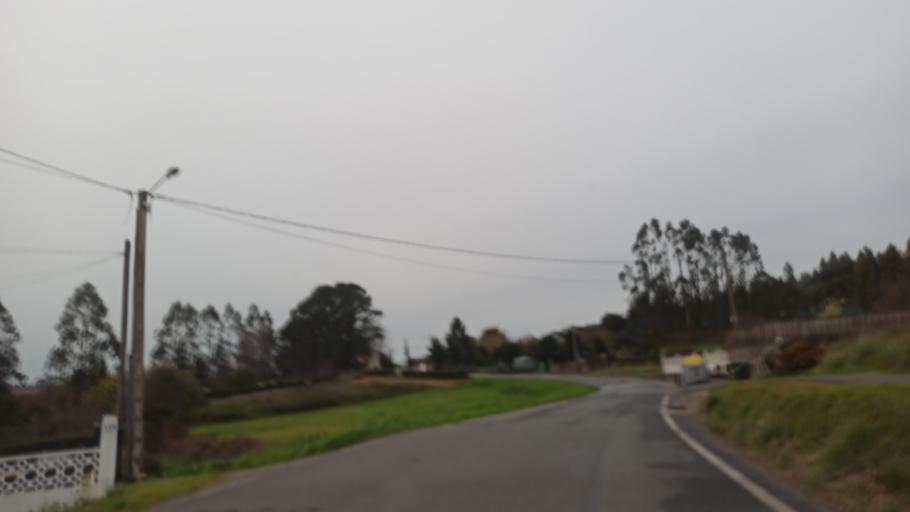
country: ES
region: Galicia
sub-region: Provincia da Coruna
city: Oleiros
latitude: 43.3929
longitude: -8.3132
